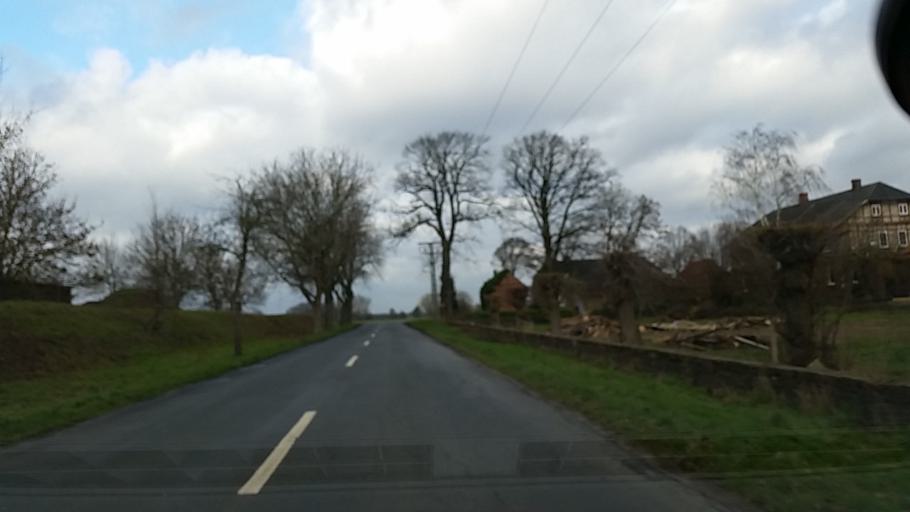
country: DE
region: Lower Saxony
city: Wittingen
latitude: 52.7070
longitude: 10.7464
